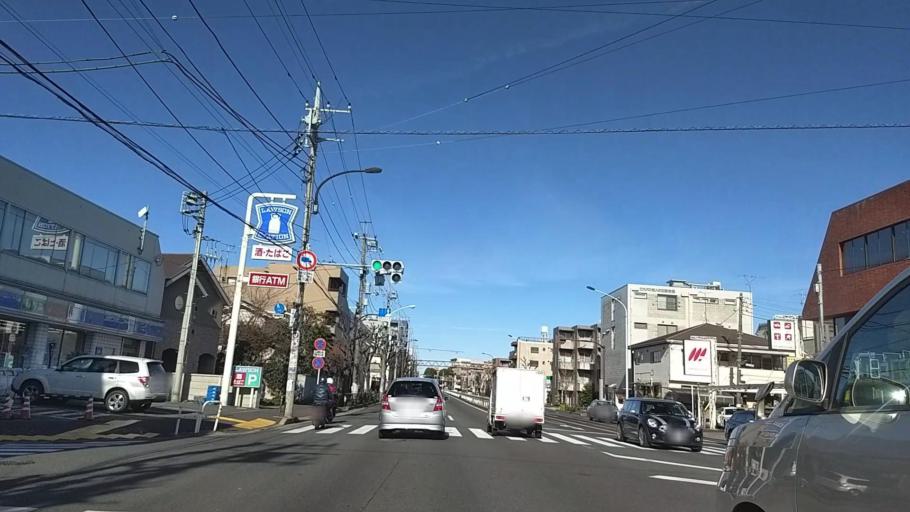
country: JP
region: Kanagawa
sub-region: Kawasaki-shi
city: Kawasaki
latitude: 35.5917
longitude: 139.6759
